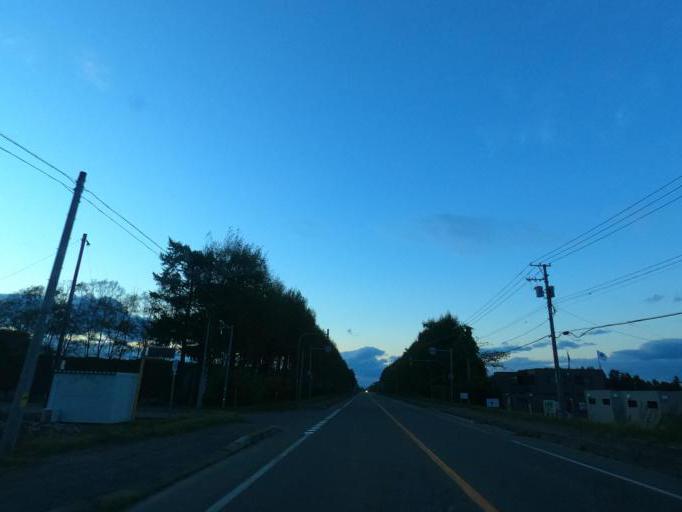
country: JP
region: Hokkaido
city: Obihiro
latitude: 42.6555
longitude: 143.1874
